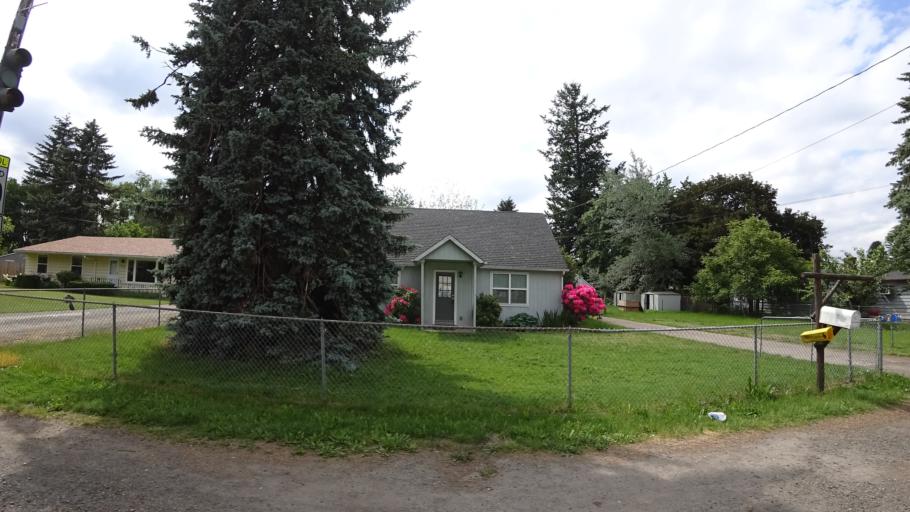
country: US
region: Oregon
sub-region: Multnomah County
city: Gresham
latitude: 45.5117
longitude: -122.4847
